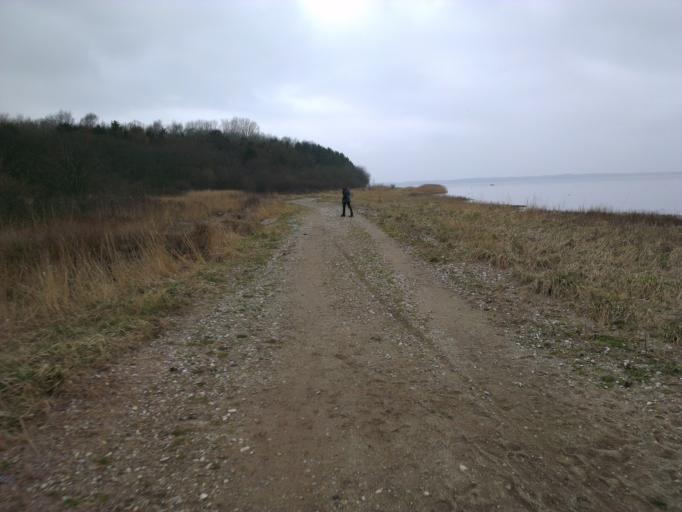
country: DK
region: Capital Region
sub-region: Frederikssund Kommune
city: Frederikssund
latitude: 55.8580
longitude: 12.0540
